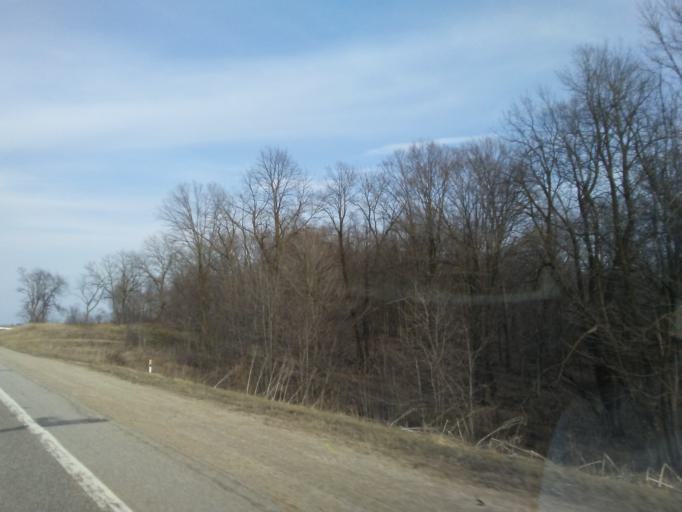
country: US
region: Wisconsin
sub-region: Grant County
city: Fennimore
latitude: 42.9908
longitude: -90.7073
